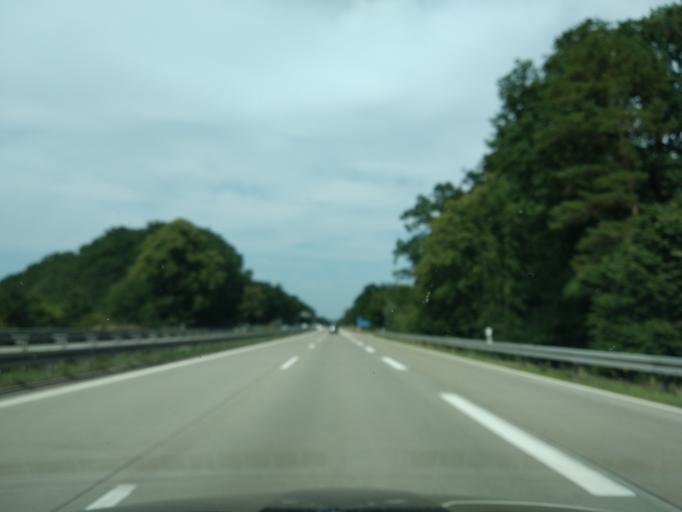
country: DE
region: Brandenburg
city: Gerswalde
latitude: 53.1262
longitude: 13.8783
